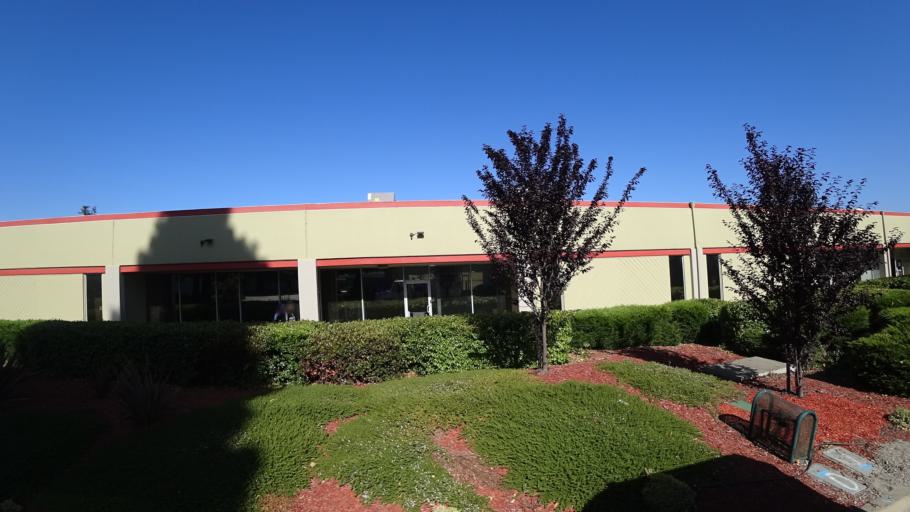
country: US
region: California
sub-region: Alameda County
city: Union City
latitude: 37.6089
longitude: -122.0511
